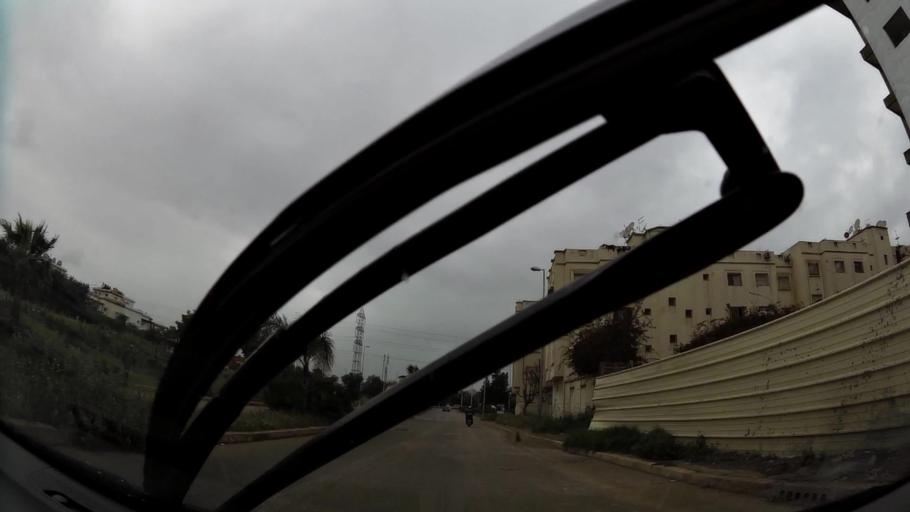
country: MA
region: Grand Casablanca
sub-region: Casablanca
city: Casablanca
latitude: 33.5262
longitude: -7.6154
